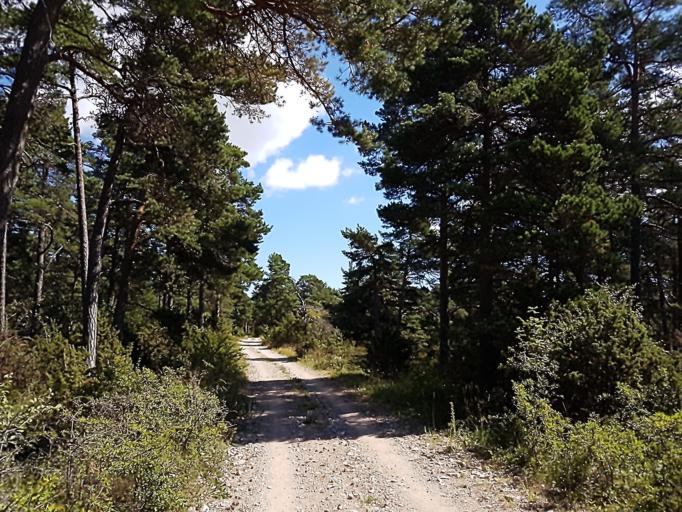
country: SE
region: Gotland
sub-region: Gotland
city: Visby
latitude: 57.6080
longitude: 18.3355
